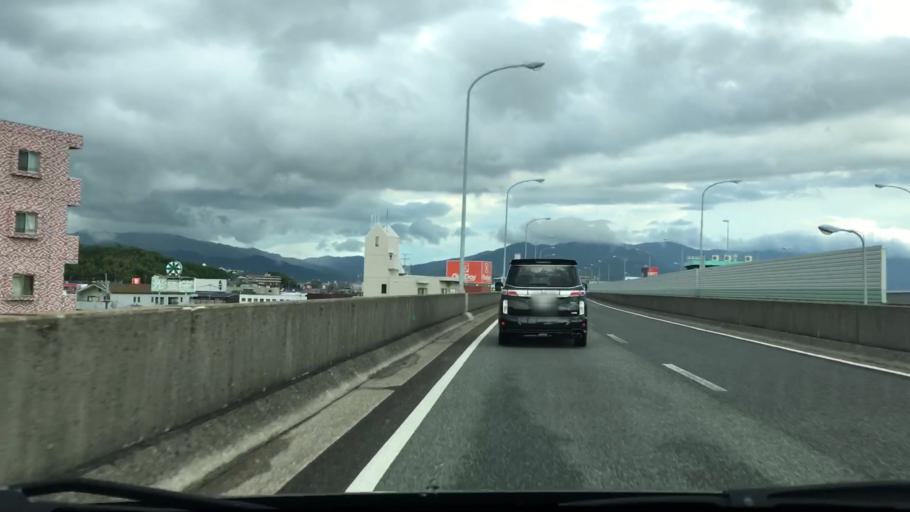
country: JP
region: Fukuoka
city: Fukuoka-shi
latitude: 33.6320
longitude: 130.4342
